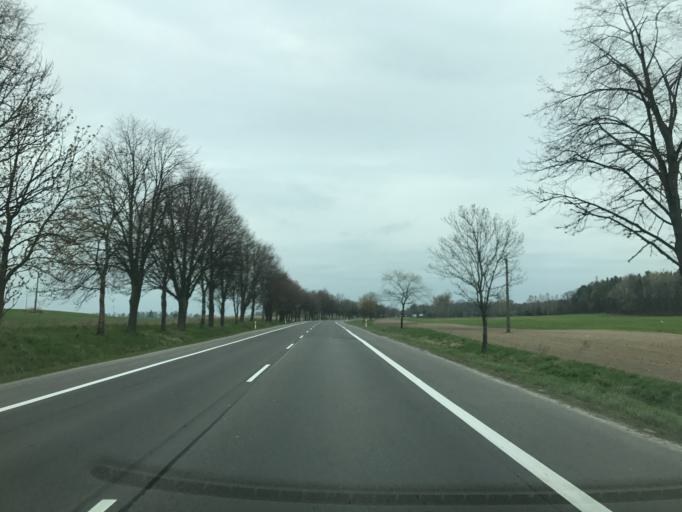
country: PL
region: Warmian-Masurian Voivodeship
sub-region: Powiat ostrodzki
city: Gierzwald
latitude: 53.6112
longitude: 20.0680
